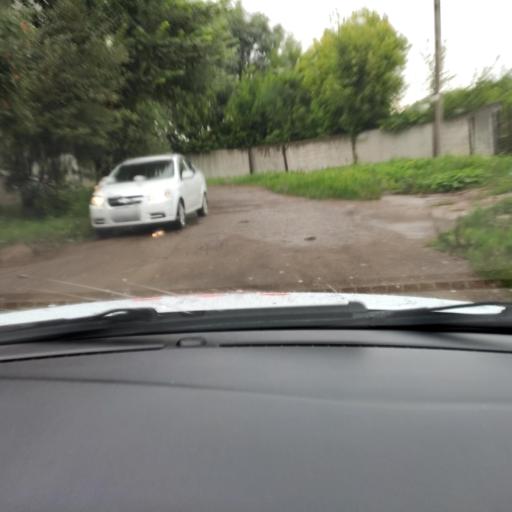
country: RU
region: Tatarstan
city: Vysokaya Gora
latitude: 55.8758
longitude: 49.2371
